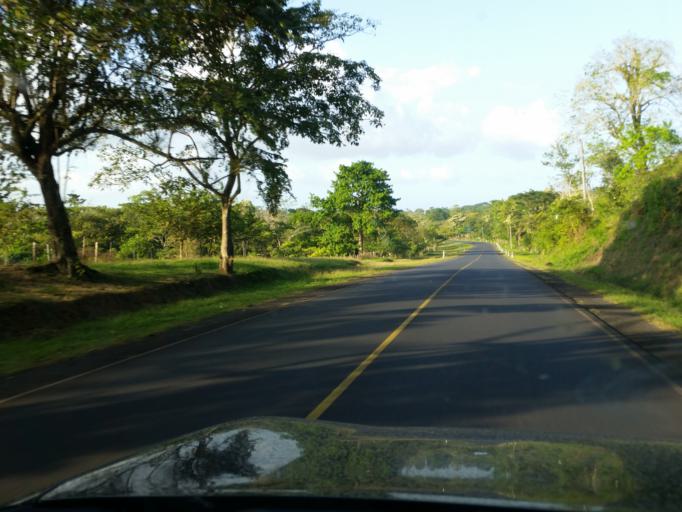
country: NI
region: Rio San Juan
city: San Carlos
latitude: 11.2713
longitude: -84.7148
